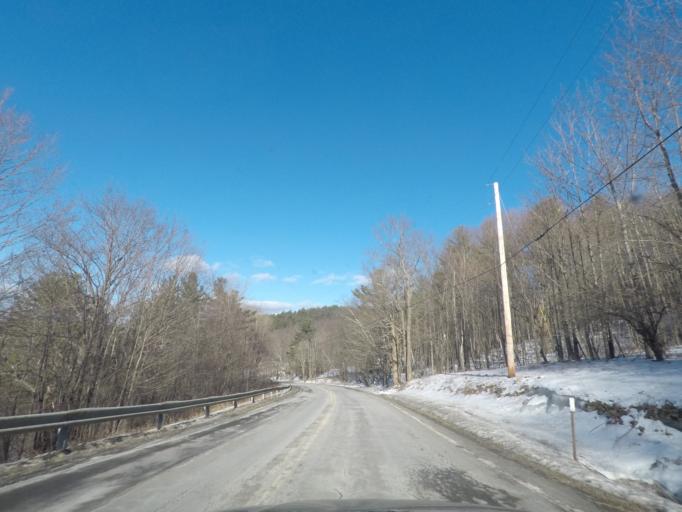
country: US
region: Massachusetts
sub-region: Berkshire County
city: Richmond
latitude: 42.3721
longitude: -73.4769
